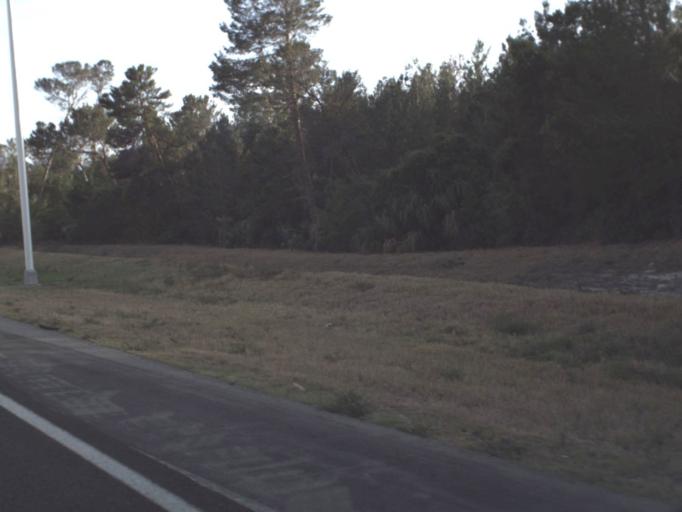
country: US
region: Florida
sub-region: Brevard County
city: Mims
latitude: 28.6217
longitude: -80.8517
